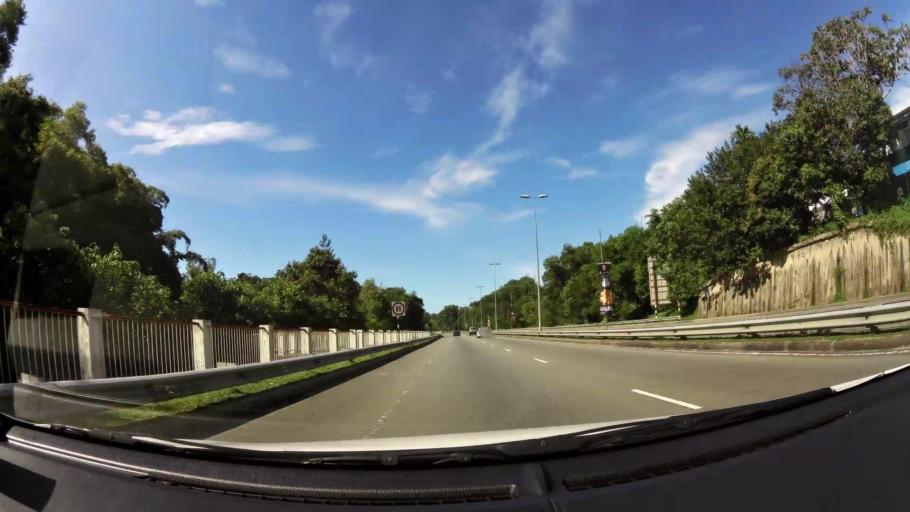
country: BN
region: Brunei and Muara
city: Bandar Seri Begawan
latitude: 4.9571
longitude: 114.9492
